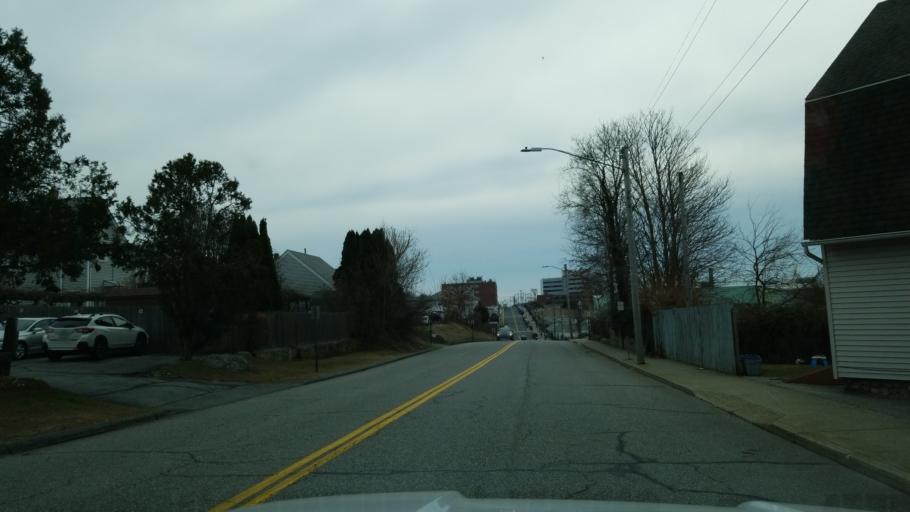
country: US
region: Connecticut
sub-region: New London County
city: Groton
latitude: 41.3499
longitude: -72.0785
